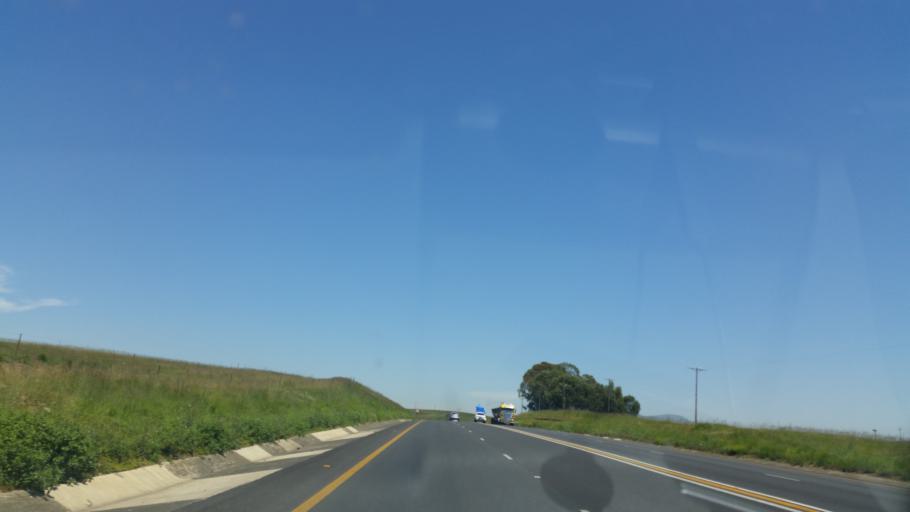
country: ZA
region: Orange Free State
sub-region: Thabo Mofutsanyana District Municipality
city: Harrismith
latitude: -28.3676
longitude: 29.3597
